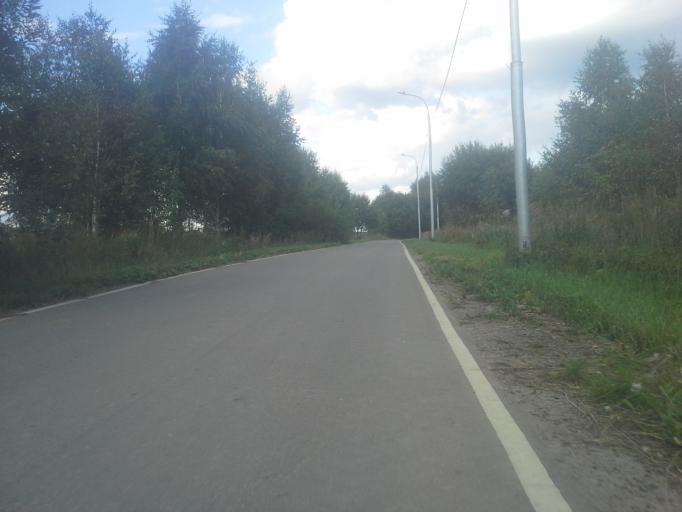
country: RU
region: Moskovskaya
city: Selyatino
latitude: 55.4340
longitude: 37.0566
